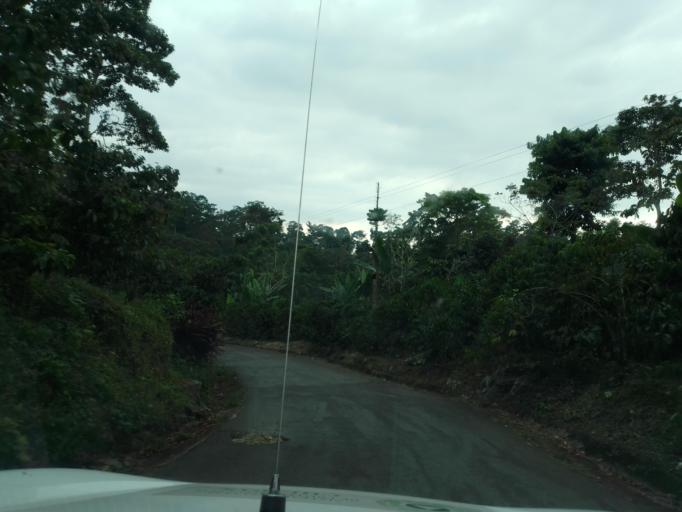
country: MX
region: Chiapas
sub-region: Union Juarez
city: Santo Domingo
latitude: 15.0519
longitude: -92.1213
